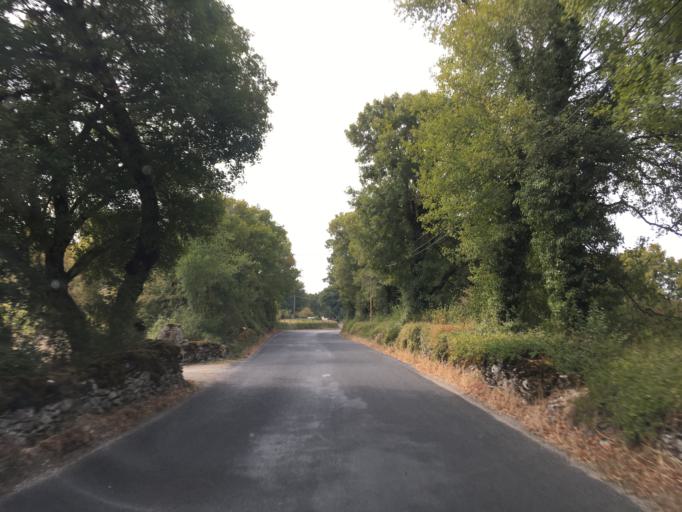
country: FR
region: Midi-Pyrenees
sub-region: Departement du Lot
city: Gramat
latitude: 44.8086
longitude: 1.6192
